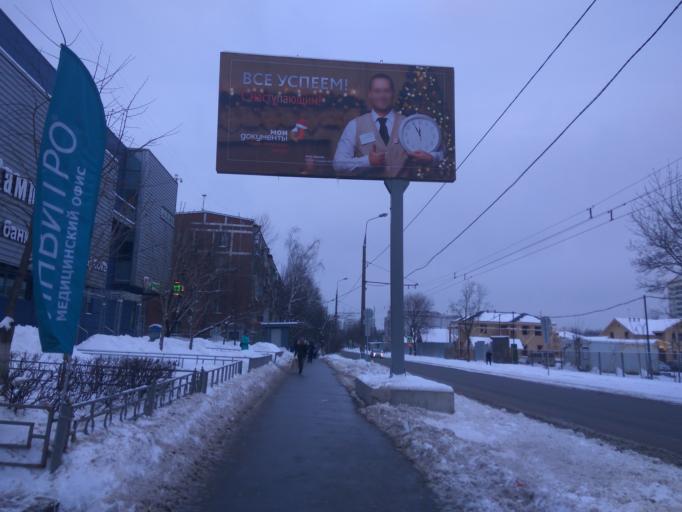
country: RU
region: Moscow
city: Novyye Kuz'minki
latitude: 55.7029
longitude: 37.7661
